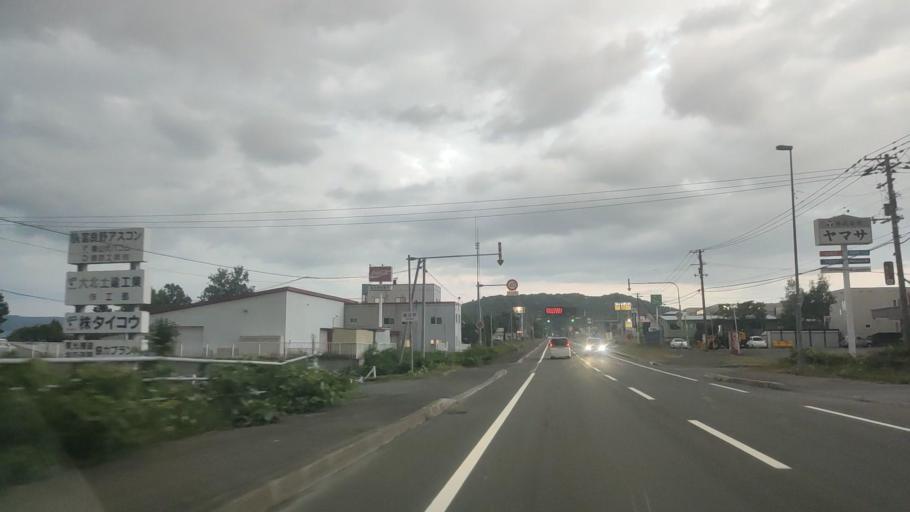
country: JP
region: Hokkaido
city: Shimo-furano
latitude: 43.3505
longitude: 142.3669
